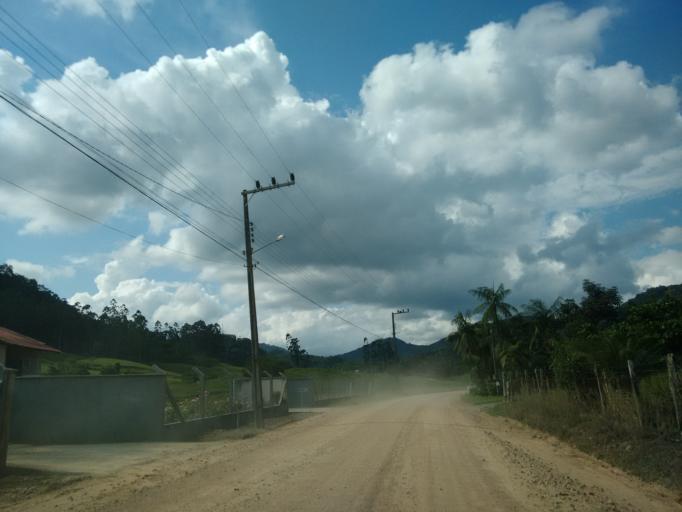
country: BR
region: Santa Catarina
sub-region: Pomerode
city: Pomerode
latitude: -26.8082
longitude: -49.1414
